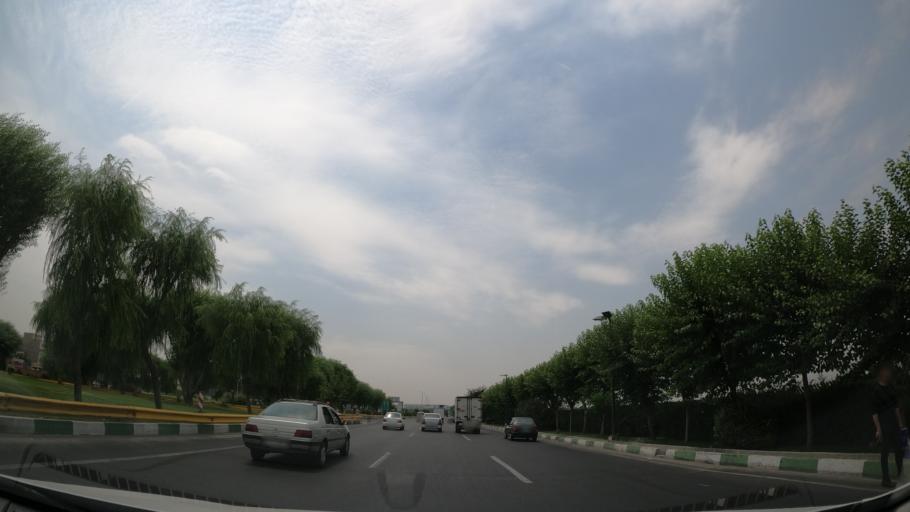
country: IR
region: Tehran
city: Tehran
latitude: 35.6802
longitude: 51.3380
